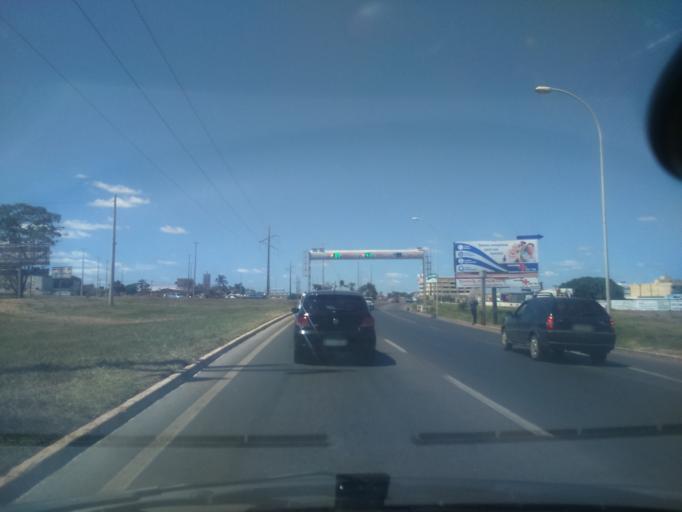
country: BR
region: Goias
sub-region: Luziania
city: Luziania
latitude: -16.0492
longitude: -48.0325
